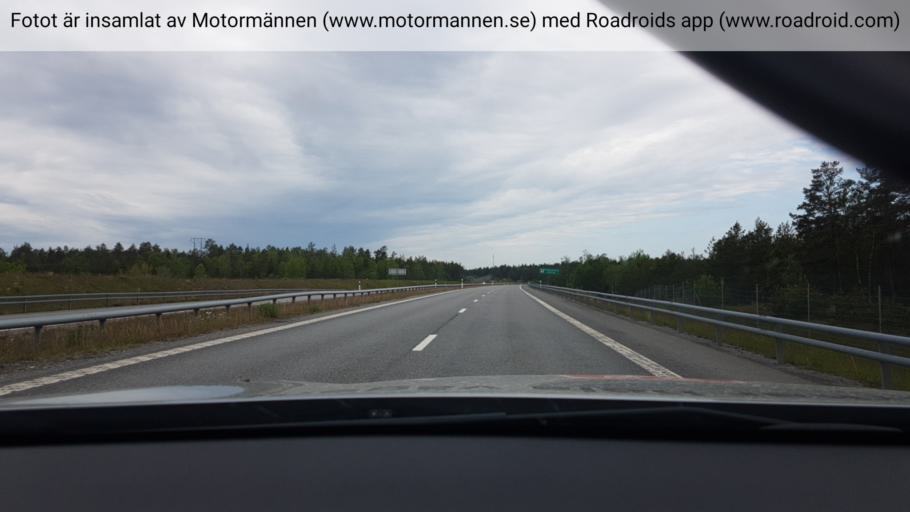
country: SE
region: Stockholm
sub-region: Nynashamns Kommun
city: Osmo
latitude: 59.0490
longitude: 17.9889
